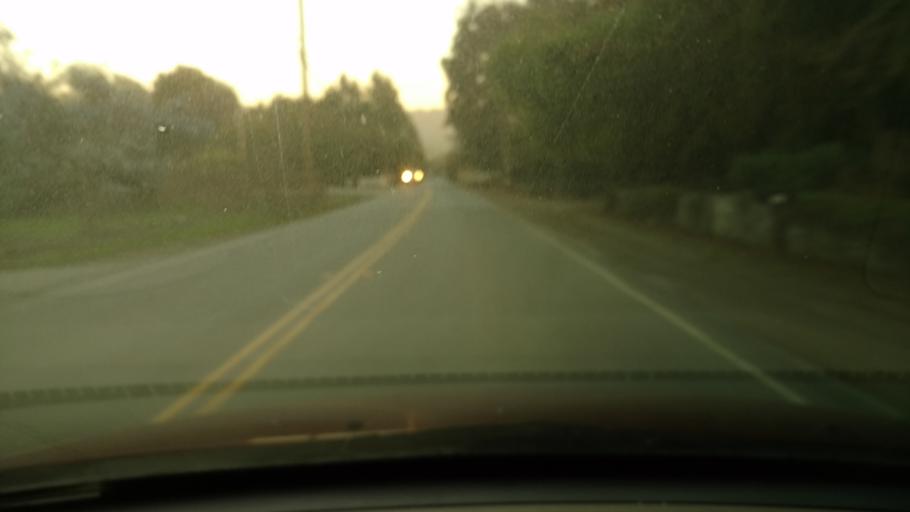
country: US
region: California
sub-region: Santa Cruz County
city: Amesti
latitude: 36.9724
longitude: -121.7613
